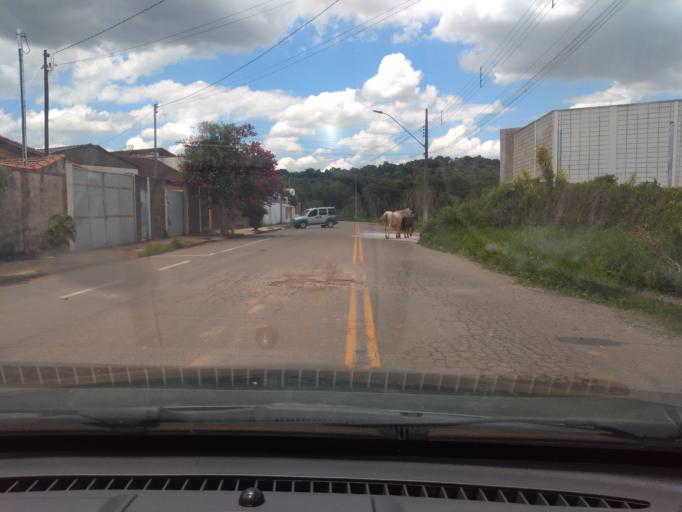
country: BR
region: Minas Gerais
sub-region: Tres Coracoes
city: Tres Coracoes
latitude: -21.6741
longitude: -45.2652
